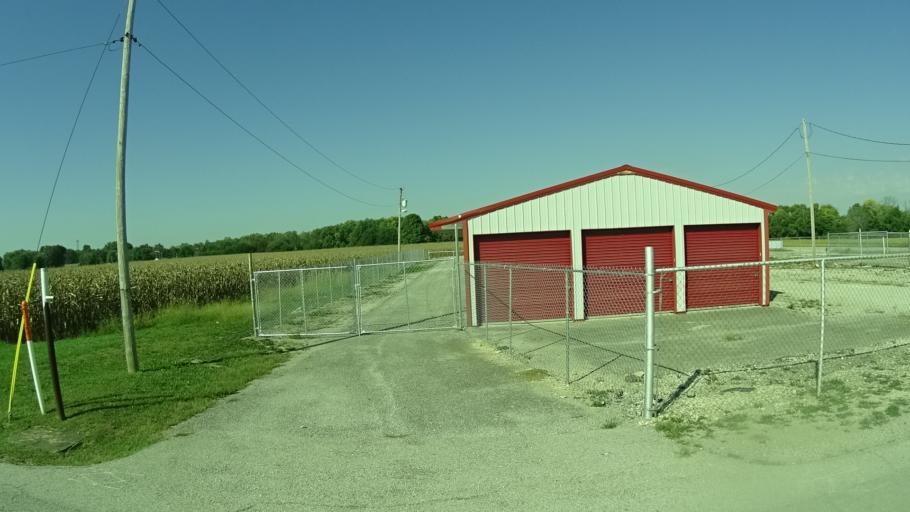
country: US
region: Indiana
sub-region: Madison County
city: Lapel
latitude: 40.0773
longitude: -85.8434
